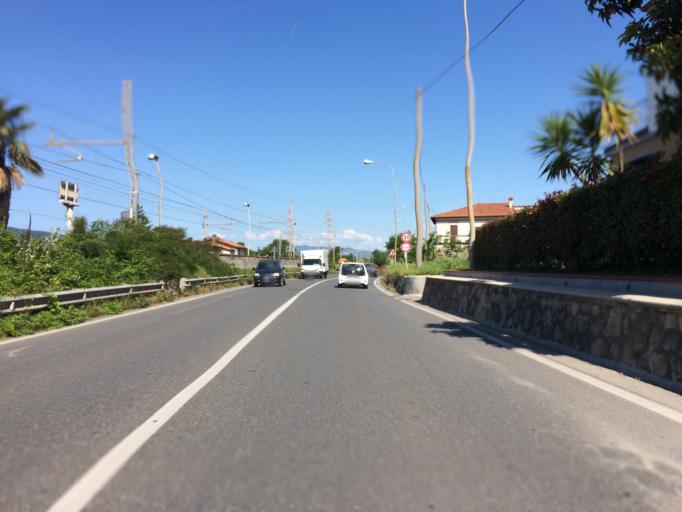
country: IT
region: Liguria
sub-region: Provincia di La Spezia
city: Colombiera-Molicciara
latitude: 44.0751
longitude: 10.0158
